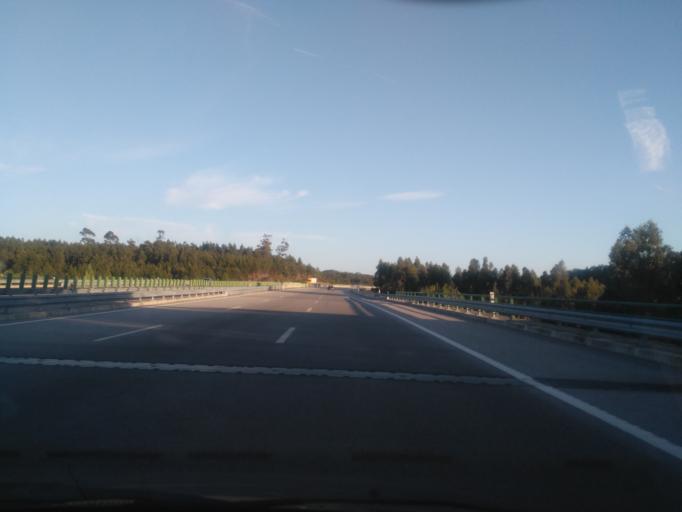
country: PT
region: Coimbra
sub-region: Figueira da Foz
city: Alhadas
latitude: 40.1148
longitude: -8.7468
